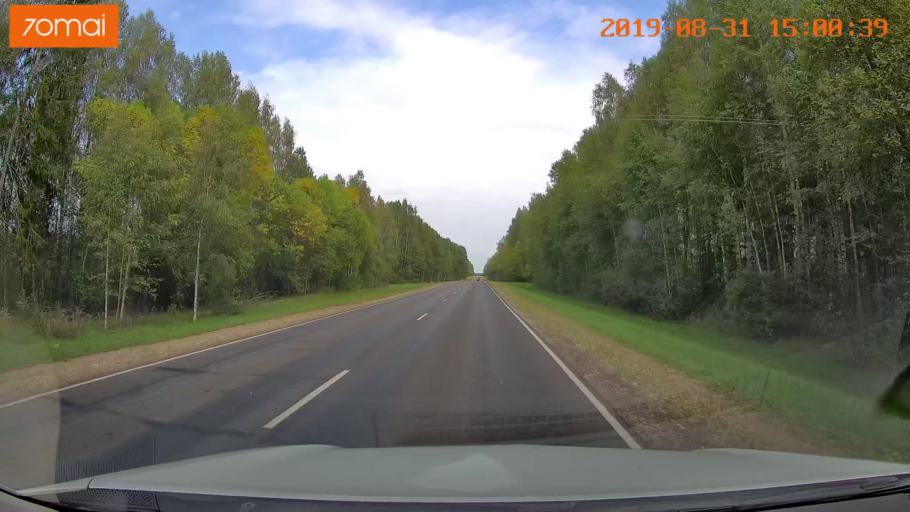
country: RU
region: Kaluga
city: Spas-Demensk
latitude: 54.3336
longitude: 34.0368
